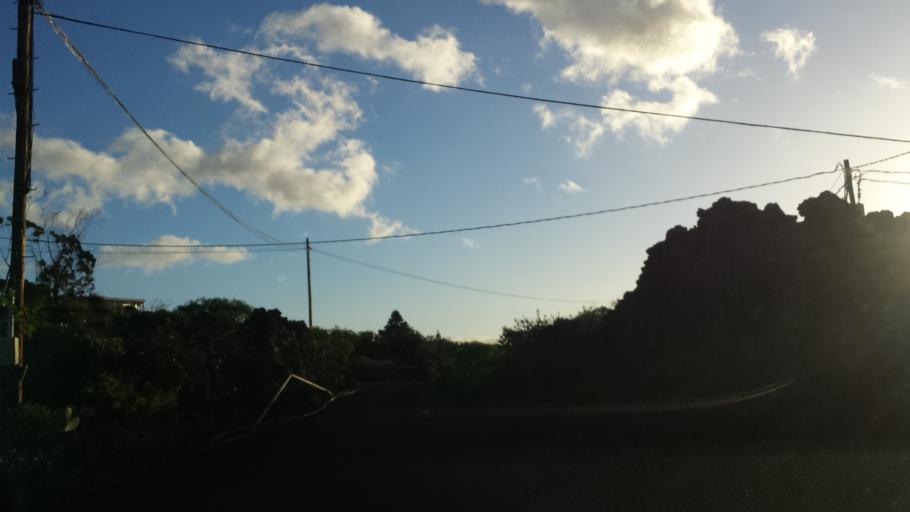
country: ES
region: Canary Islands
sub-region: Provincia de Santa Cruz de Tenerife
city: El Paso
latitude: 28.6120
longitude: -17.8917
